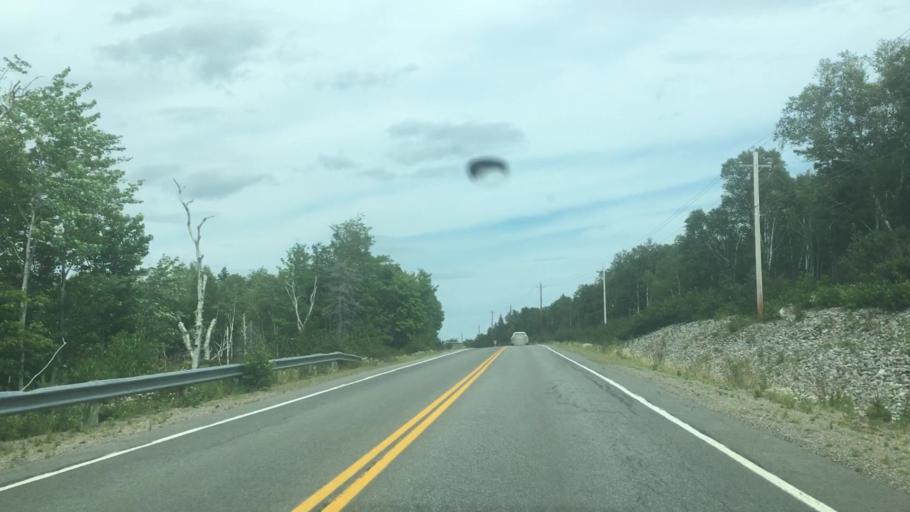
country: CA
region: Nova Scotia
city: Sydney Mines
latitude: 46.5023
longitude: -60.4374
